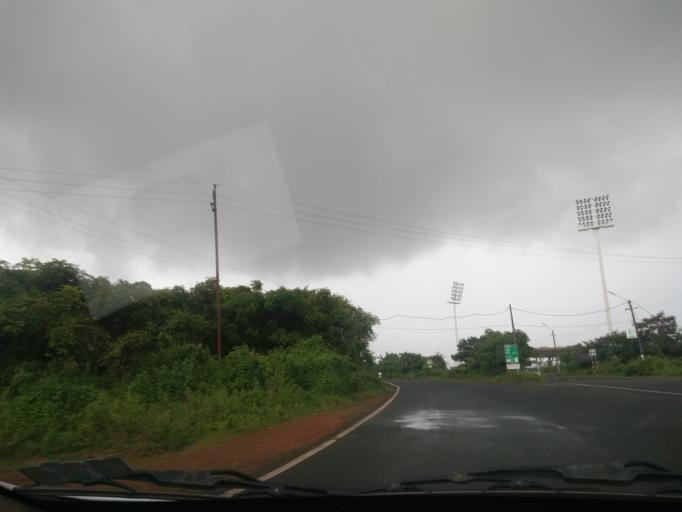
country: IN
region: Goa
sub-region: North Goa
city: Bambolim
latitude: 15.4665
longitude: 73.8640
